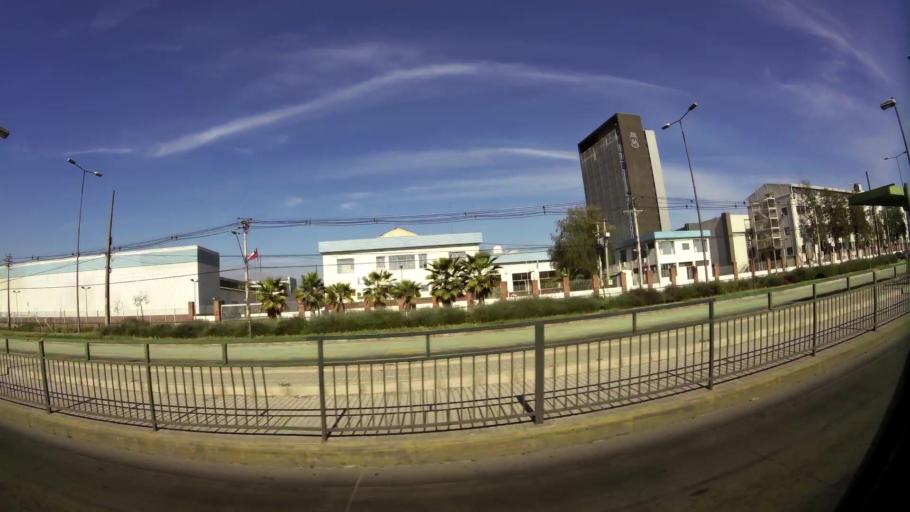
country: CL
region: Santiago Metropolitan
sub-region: Provincia de Santiago
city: Lo Prado
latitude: -33.4887
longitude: -70.7008
